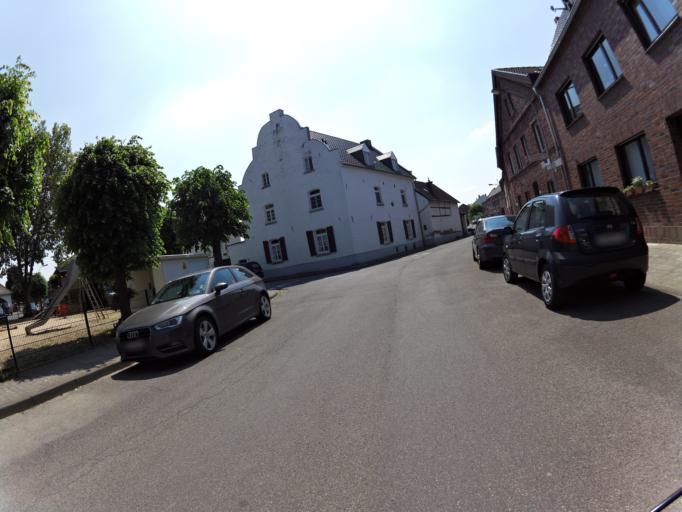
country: DE
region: North Rhine-Westphalia
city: Niedermerz
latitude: 50.9060
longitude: 6.2550
